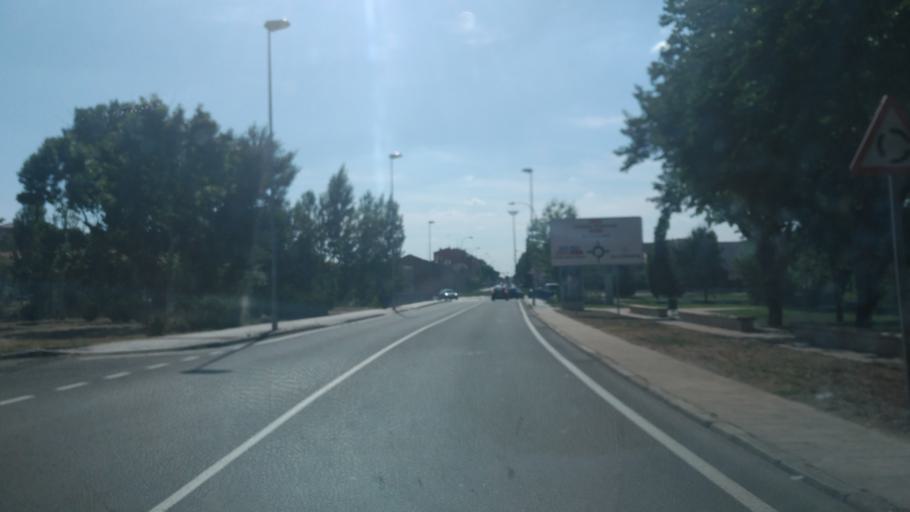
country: ES
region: Castille and Leon
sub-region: Provincia de Salamanca
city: Salamanca
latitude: 40.9551
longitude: -5.6745
